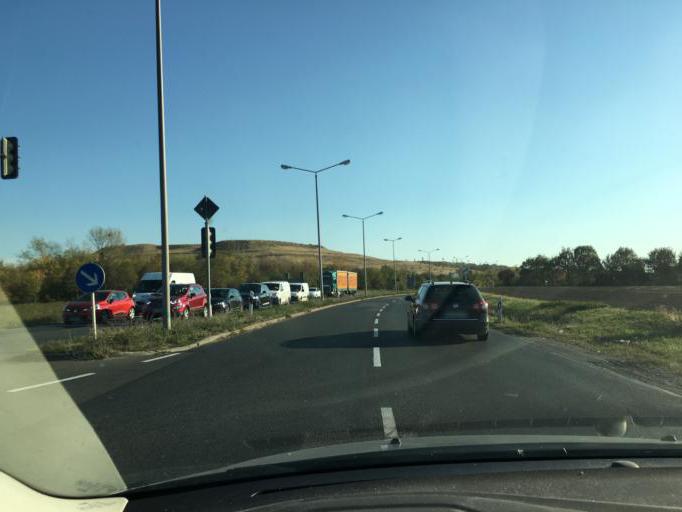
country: DE
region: Saxony
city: Rackwitz
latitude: 51.4157
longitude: 12.3960
